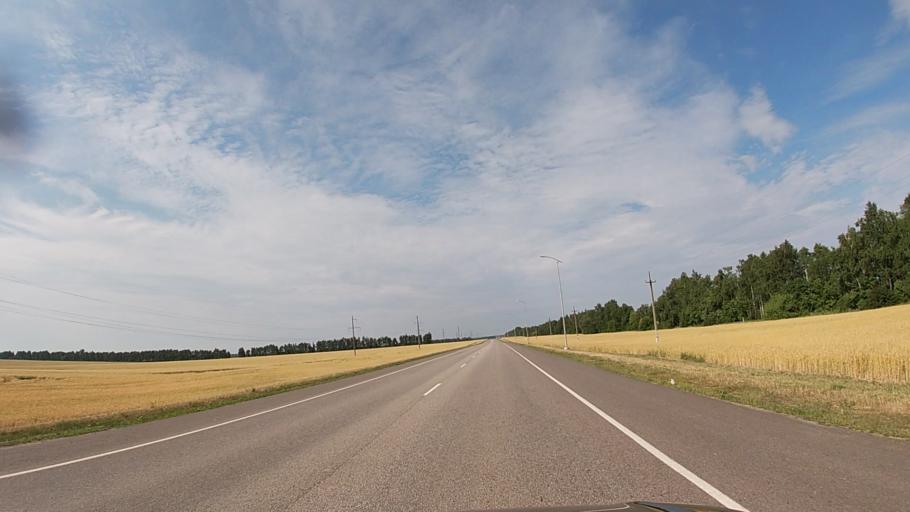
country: RU
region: Belgorod
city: Proletarskiy
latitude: 50.8265
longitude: 35.7609
